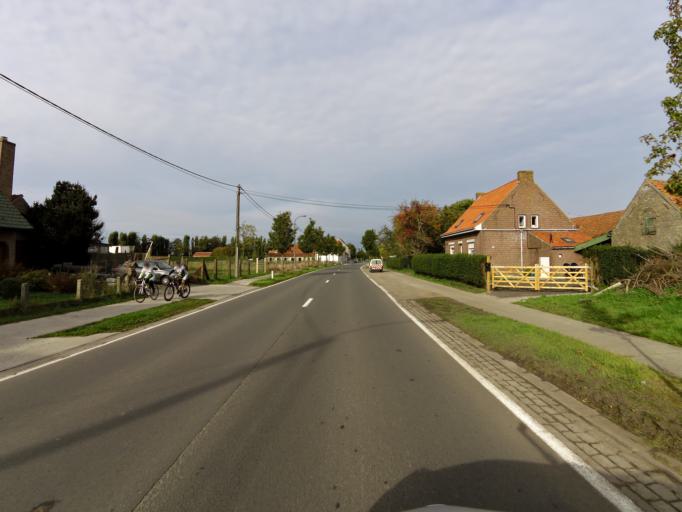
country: BE
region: Flanders
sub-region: Provincie West-Vlaanderen
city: Oudenburg
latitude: 51.1442
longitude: 3.0249
